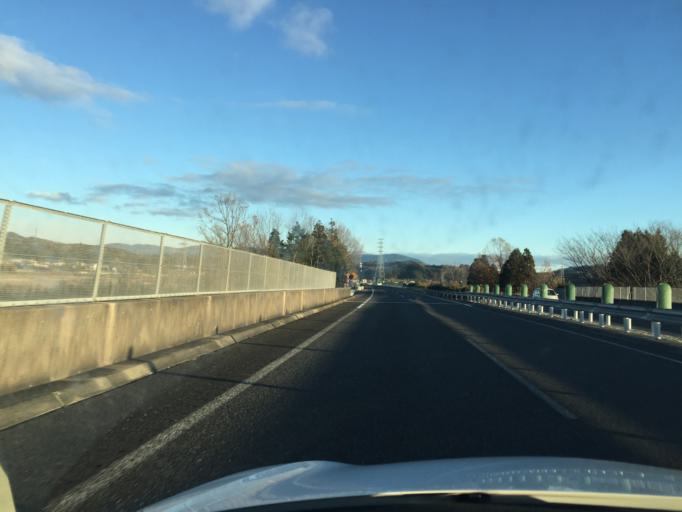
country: JP
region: Ibaraki
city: Kitaibaraki
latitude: 36.9175
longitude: 140.7589
